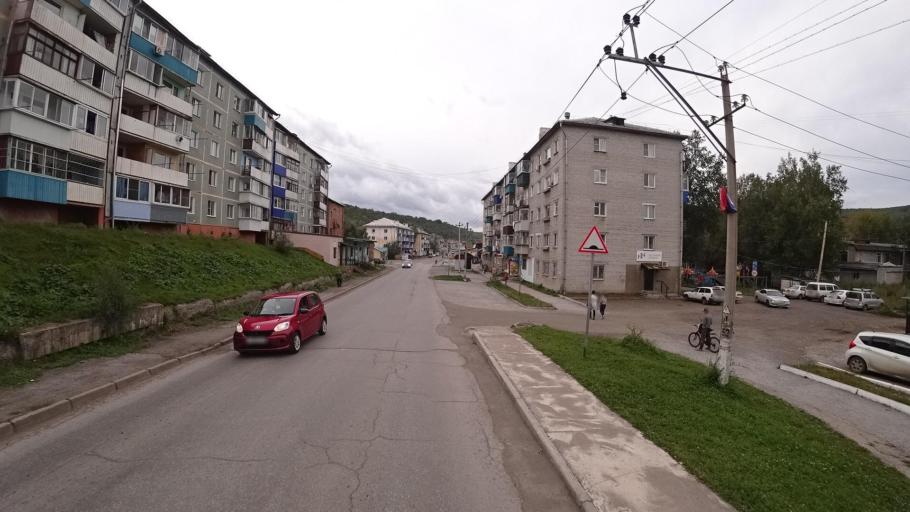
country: RU
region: Jewish Autonomous Oblast
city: Khingansk
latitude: 49.0125
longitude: 131.0566
